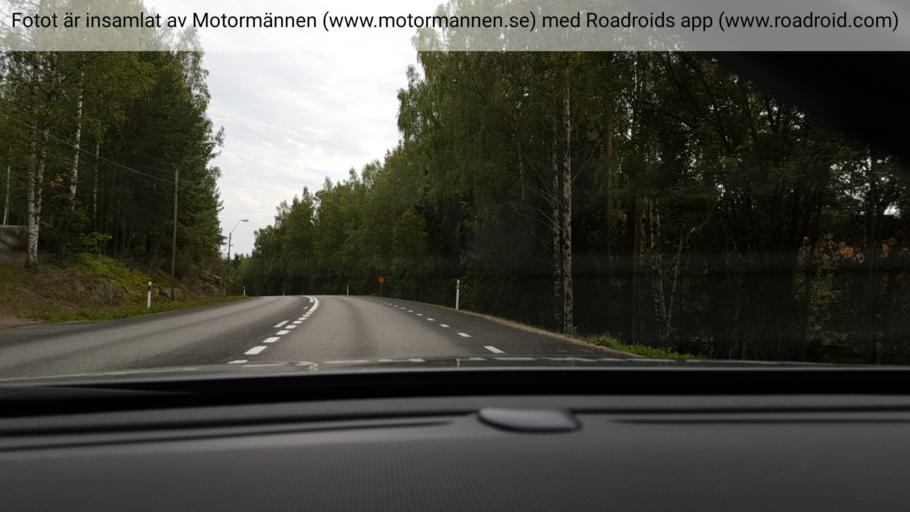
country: SE
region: Dalarna
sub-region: Faluns Kommun
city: Grycksbo
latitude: 60.6908
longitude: 15.4882
